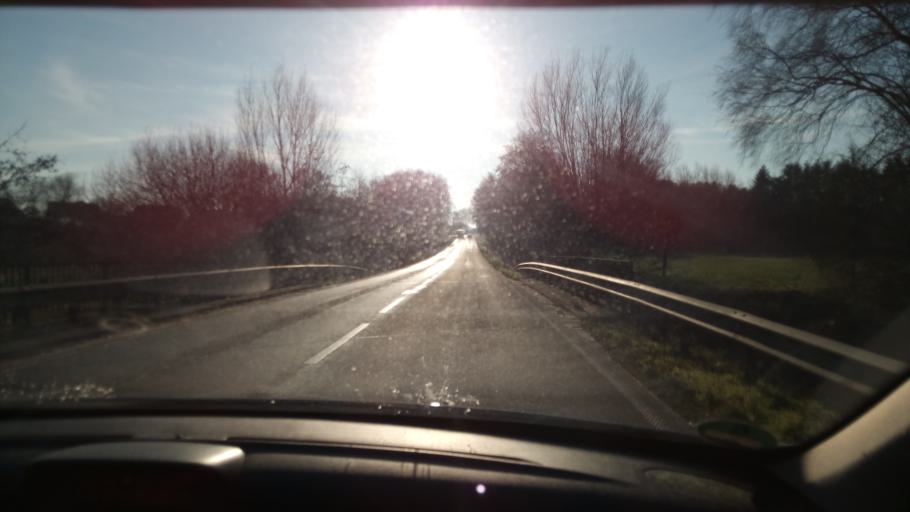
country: DE
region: Schleswig-Holstein
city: Witzeeze
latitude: 53.4508
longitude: 10.6123
